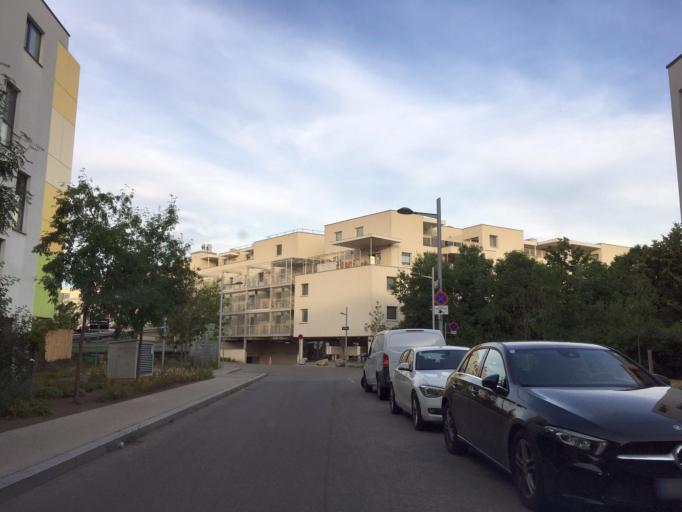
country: AT
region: Lower Austria
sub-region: Politischer Bezirk Wien-Umgebung
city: Gerasdorf bei Wien
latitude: 48.2186
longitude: 16.4497
